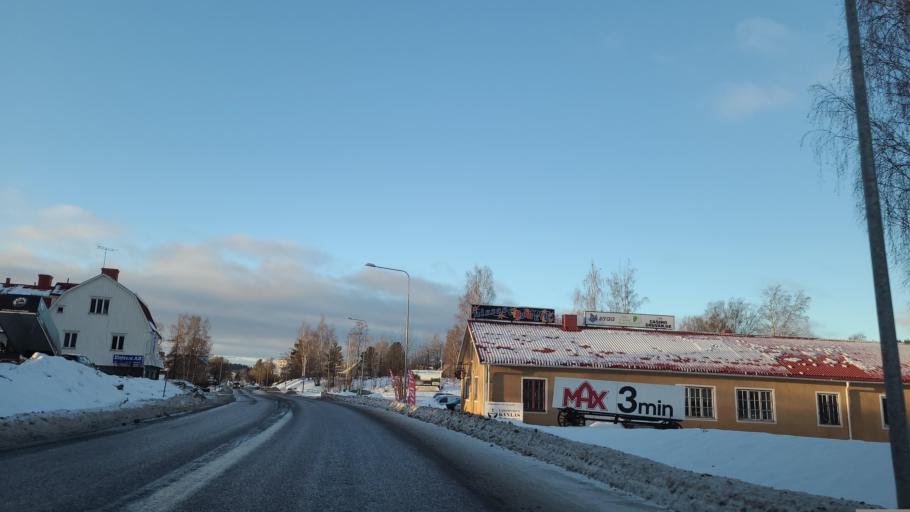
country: SE
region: Gaevleborg
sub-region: Bollnas Kommun
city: Bollnas
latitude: 61.3567
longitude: 16.4148
